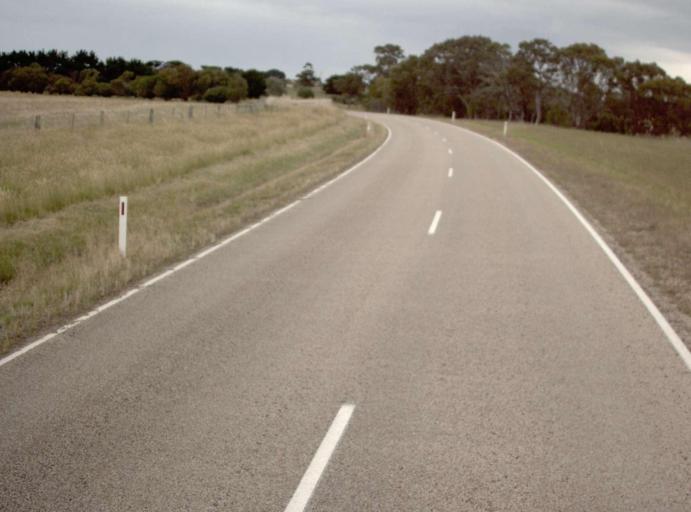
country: AU
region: Victoria
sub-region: East Gippsland
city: Bairnsdale
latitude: -37.9736
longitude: 147.4662
